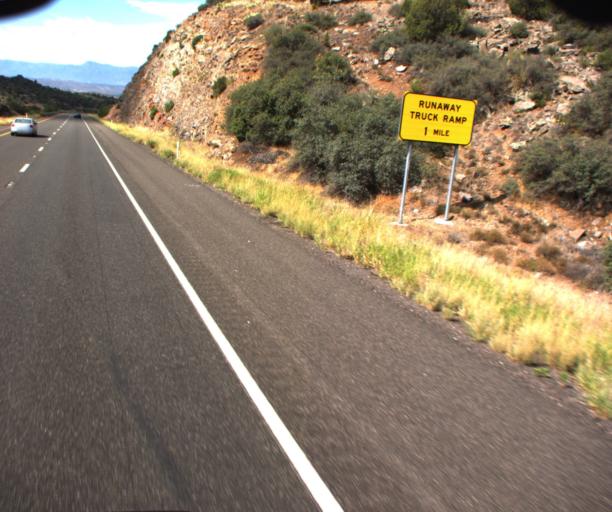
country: US
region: Arizona
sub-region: Yavapai County
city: Big Park
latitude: 34.7175
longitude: -111.7264
